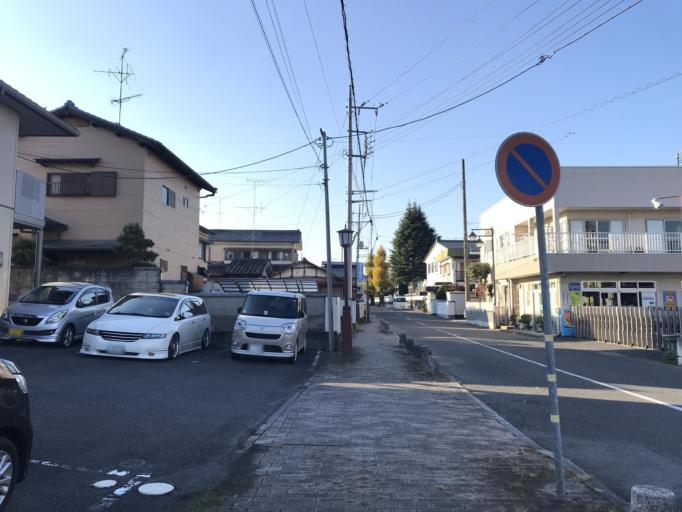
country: JP
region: Ibaraki
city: Yuki
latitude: 36.3045
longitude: 139.8784
